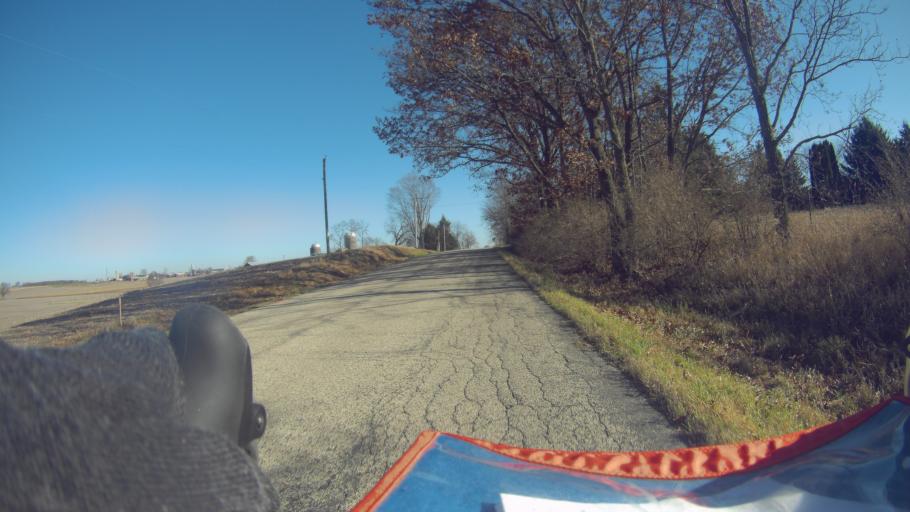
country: US
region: Wisconsin
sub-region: Green County
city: Brooklyn
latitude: 42.8708
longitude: -89.4212
